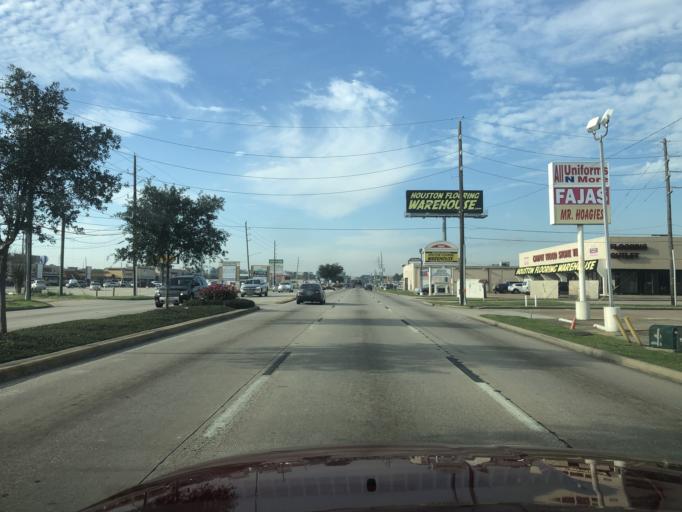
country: US
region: Texas
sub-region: Harris County
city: Spring
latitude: 30.0090
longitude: -95.4603
